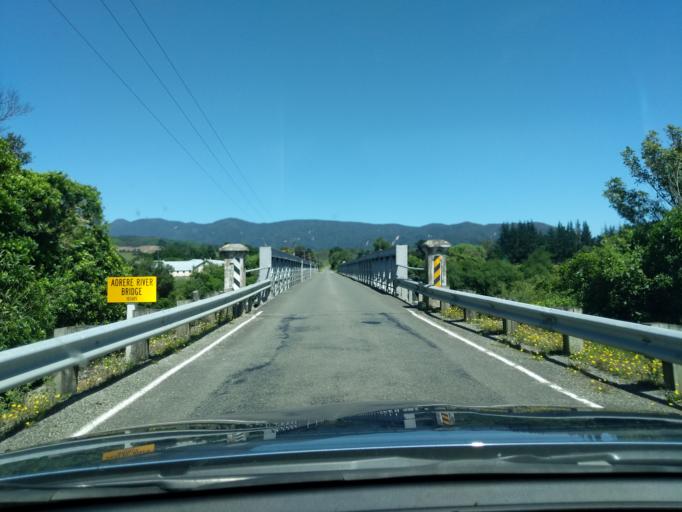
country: NZ
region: Tasman
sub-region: Tasman District
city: Takaka
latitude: -40.7292
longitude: 172.6293
